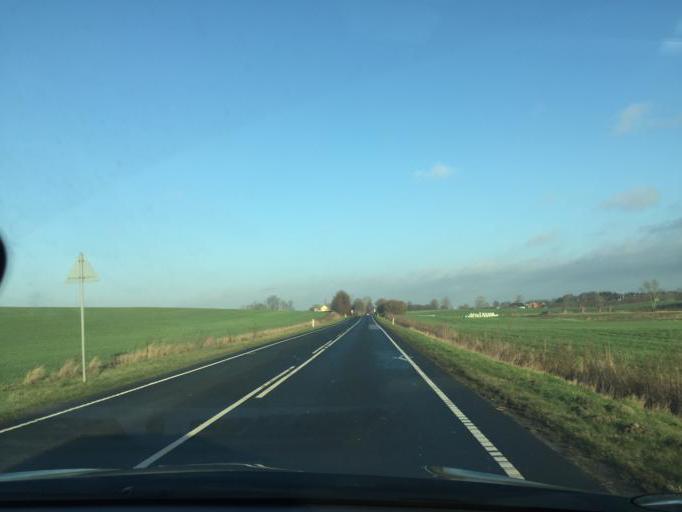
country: DK
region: South Denmark
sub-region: Faaborg-Midtfyn Kommune
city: Faaborg
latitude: 55.1742
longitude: 10.2907
